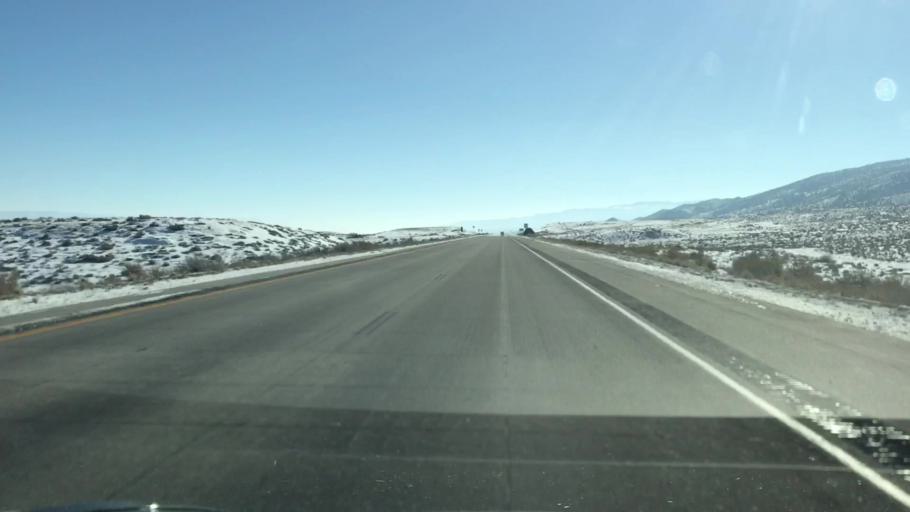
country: US
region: Colorado
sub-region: Mesa County
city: Loma
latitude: 39.2080
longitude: -108.8615
